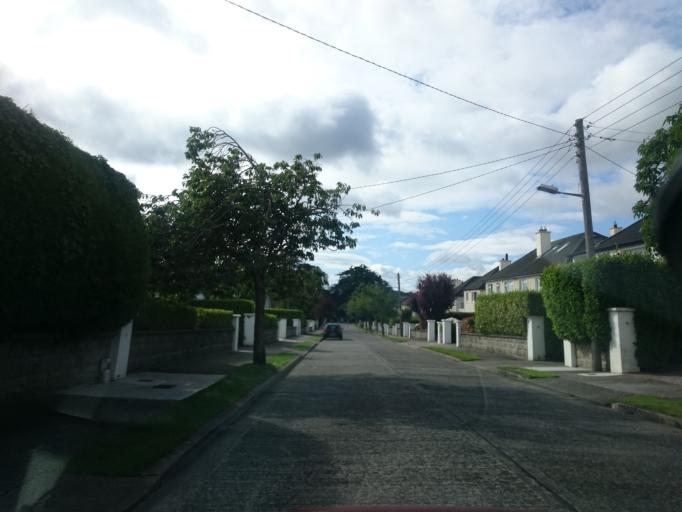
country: IE
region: Leinster
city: Mount Merrion
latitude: 53.2909
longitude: -6.2080
